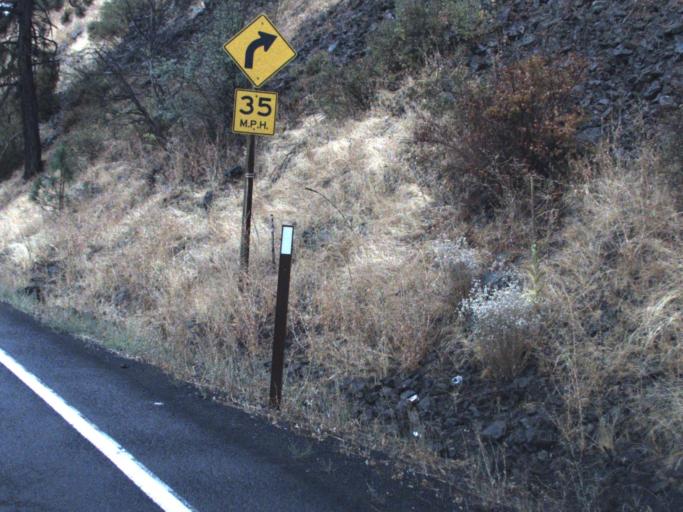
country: US
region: Washington
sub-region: Spokane County
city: Medical Lake
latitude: 47.7402
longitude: -117.8796
